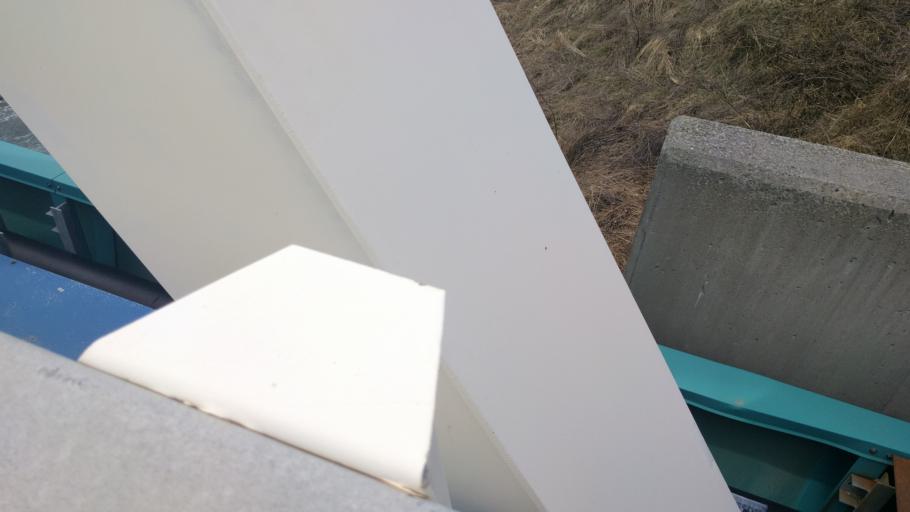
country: FR
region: Rhone-Alpes
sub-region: Departement de la Savoie
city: Modane
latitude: 45.2025
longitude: 6.5931
